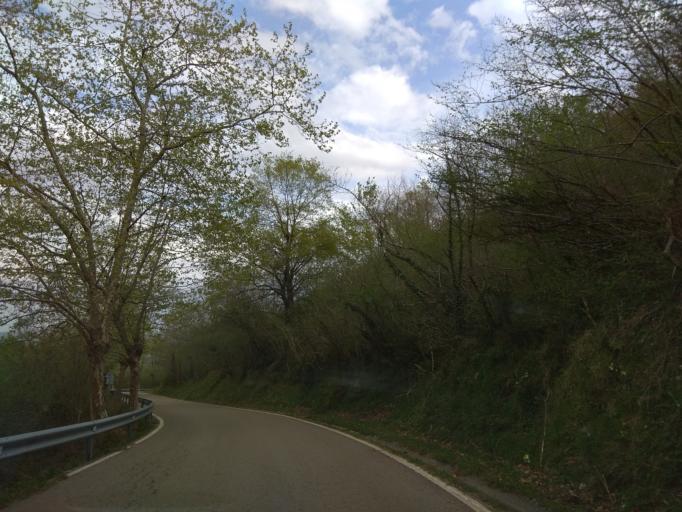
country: ES
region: Cantabria
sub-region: Provincia de Cantabria
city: San Vicente de la Barquera
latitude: 43.2547
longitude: -4.4428
